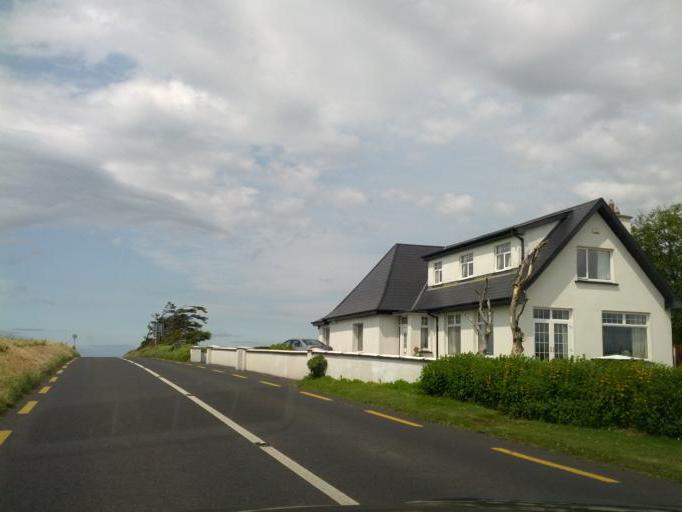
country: IE
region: Munster
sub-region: An Clar
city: Kilrush
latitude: 52.7953
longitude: -9.4450
